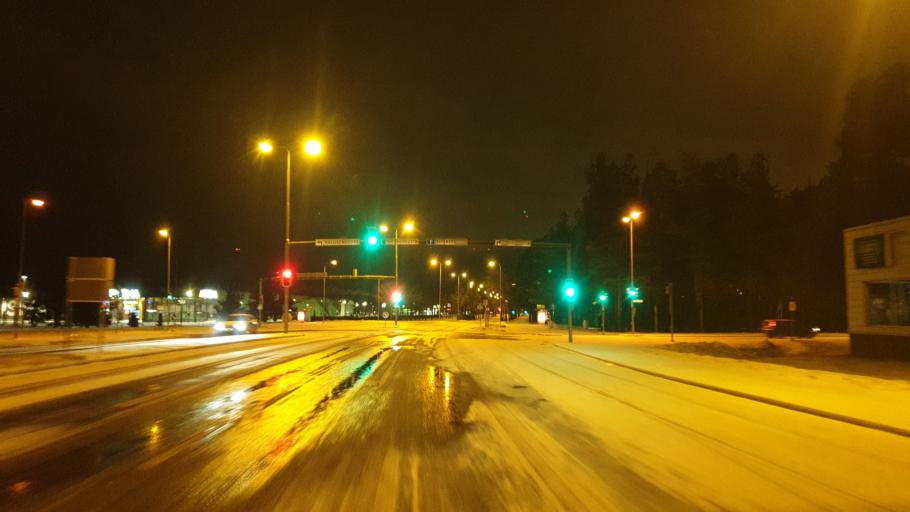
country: FI
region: Northern Ostrobothnia
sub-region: Oulu
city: Oulu
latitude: 64.9918
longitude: 25.4656
